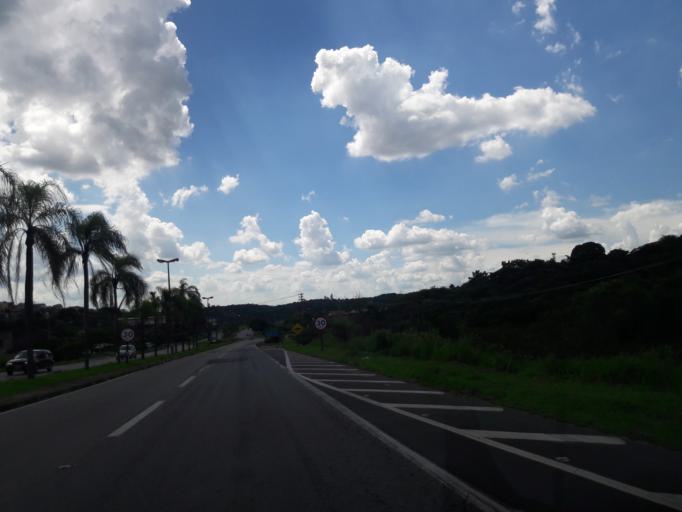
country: BR
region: Sao Paulo
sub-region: Campo Limpo Paulista
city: Campo Limpo Paulista
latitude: -23.2107
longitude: -46.7924
